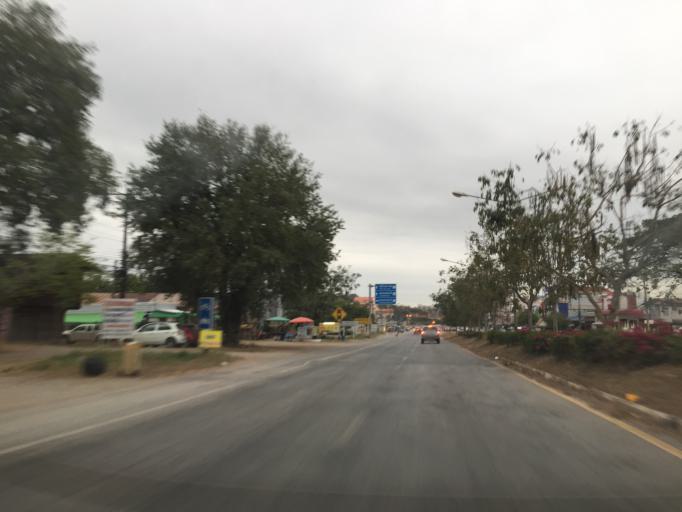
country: TH
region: Loei
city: Erawan
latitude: 17.3025
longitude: 101.9542
